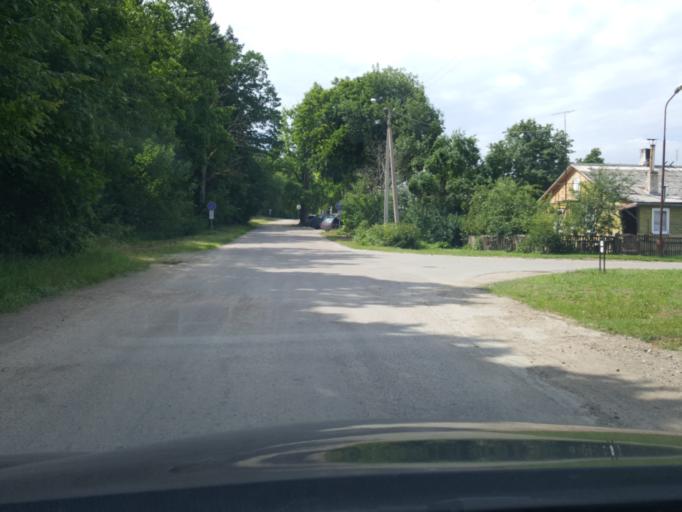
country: LT
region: Alytaus apskritis
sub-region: Alytus
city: Alytus
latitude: 54.3848
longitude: 24.0387
